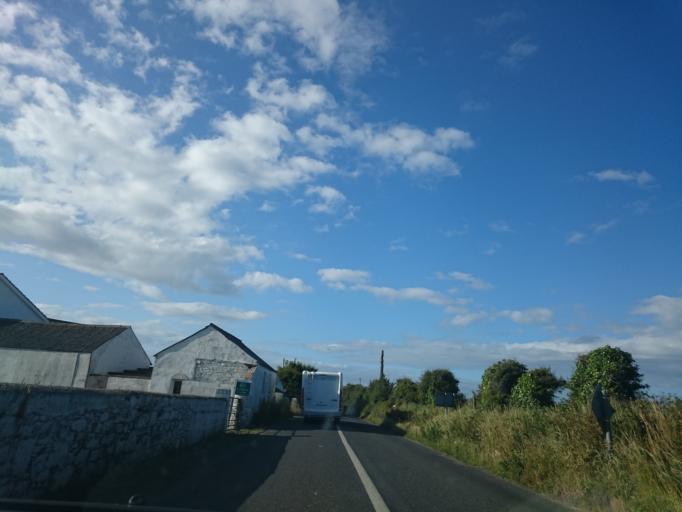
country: IE
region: Leinster
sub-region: Loch Garman
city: Loch Garman
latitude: 52.1885
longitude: -6.5619
